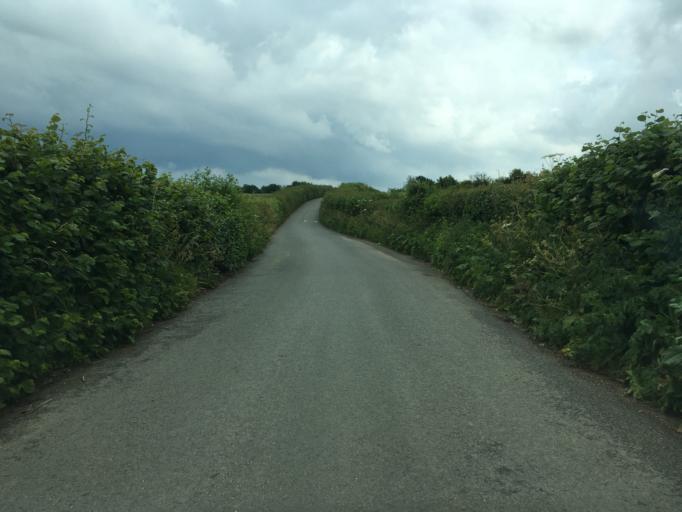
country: GB
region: England
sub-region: Gloucestershire
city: Shurdington
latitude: 51.8175
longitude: -2.0980
